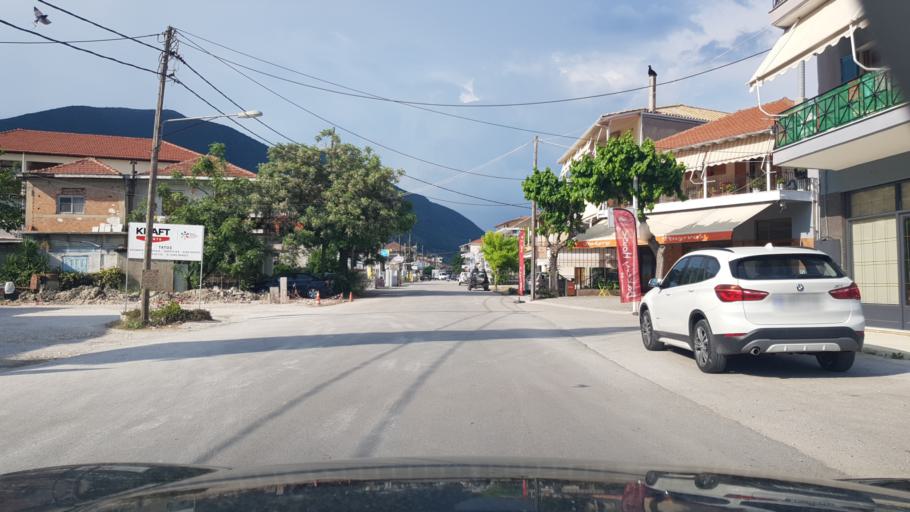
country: GR
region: Ionian Islands
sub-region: Lefkada
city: Nidri
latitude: 38.7026
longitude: 20.7067
